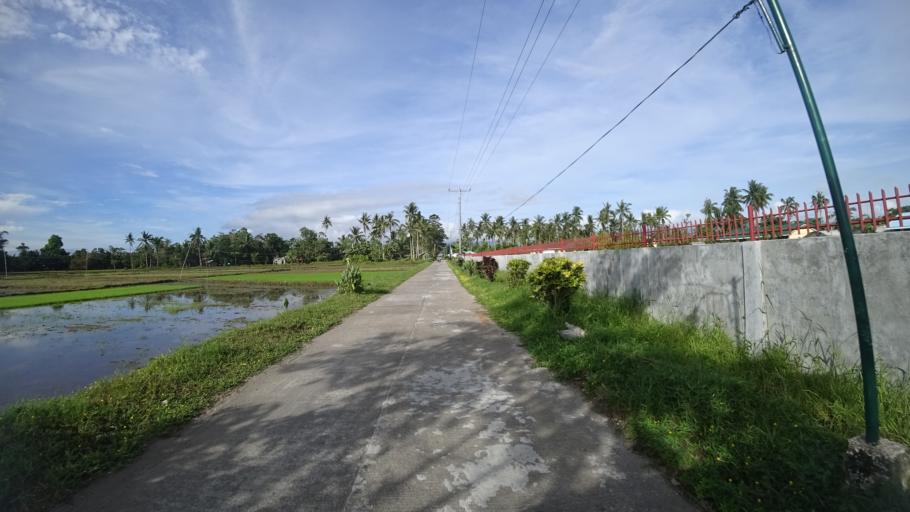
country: PH
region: Eastern Visayas
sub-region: Province of Leyte
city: Pastrana
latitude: 11.1569
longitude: 124.8617
